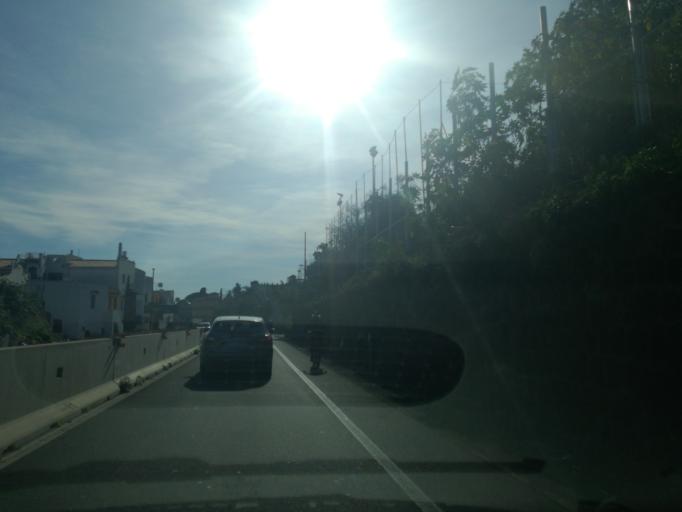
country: IT
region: Sicily
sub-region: Catania
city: Acireale
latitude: 37.6079
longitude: 15.1690
